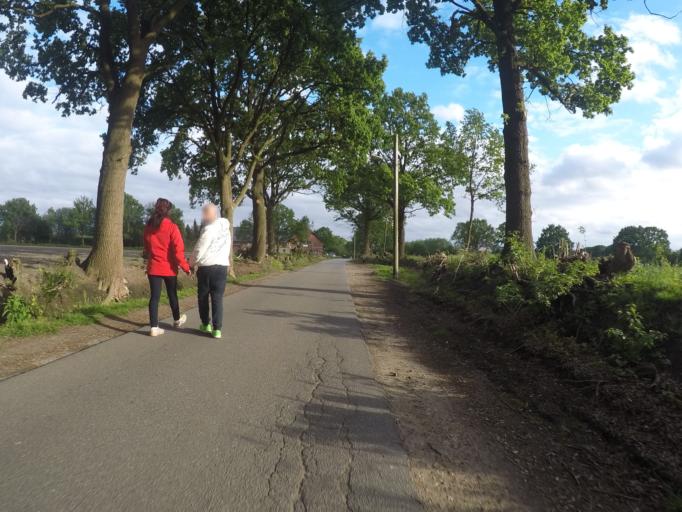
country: DE
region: Schleswig-Holstein
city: Hasloh
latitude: 53.6913
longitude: 9.9225
